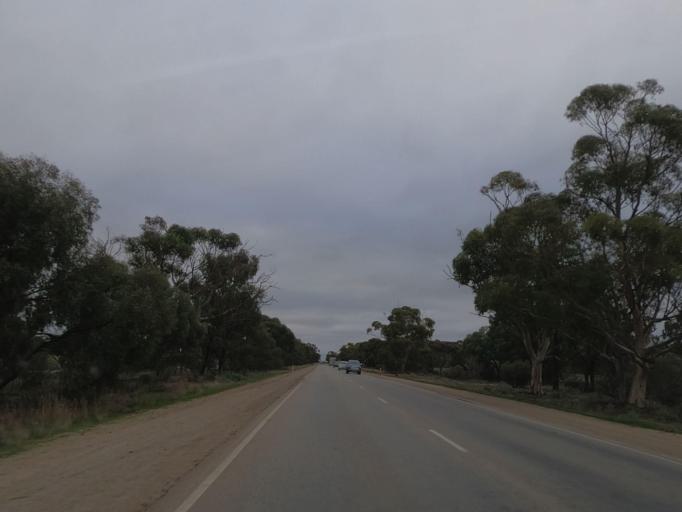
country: AU
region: Victoria
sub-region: Swan Hill
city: Swan Hill
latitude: -35.4042
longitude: 143.5799
